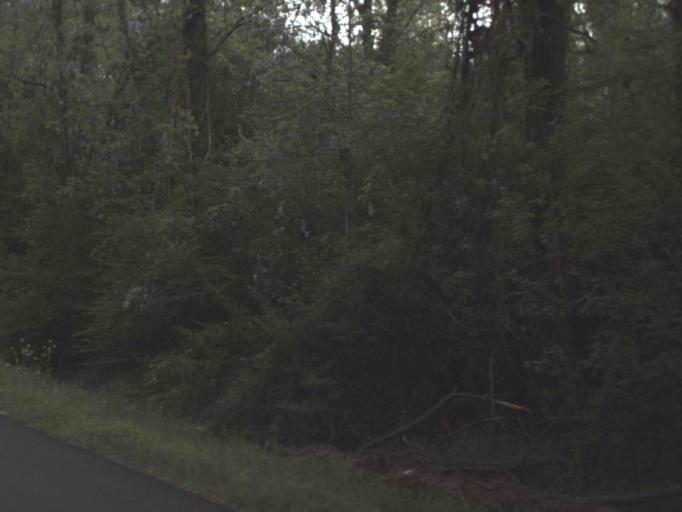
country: US
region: Alabama
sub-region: Covington County
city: Florala
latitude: 30.9674
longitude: -86.4469
